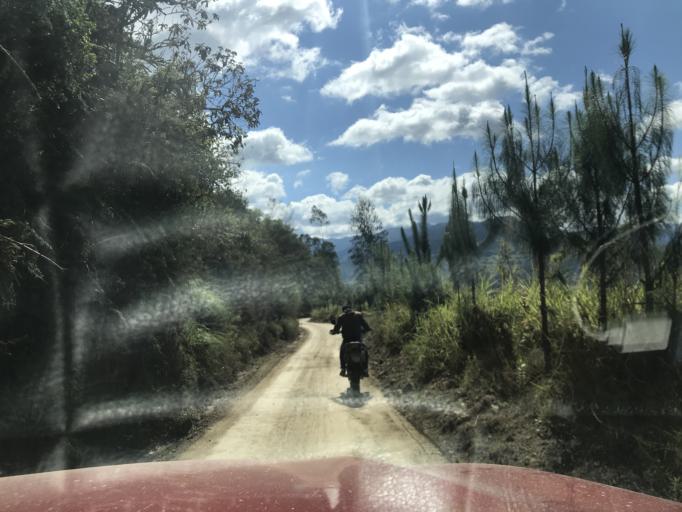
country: PE
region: Cajamarca
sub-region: Provincia de Chota
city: Querocoto
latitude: -6.3334
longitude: -79.0720
